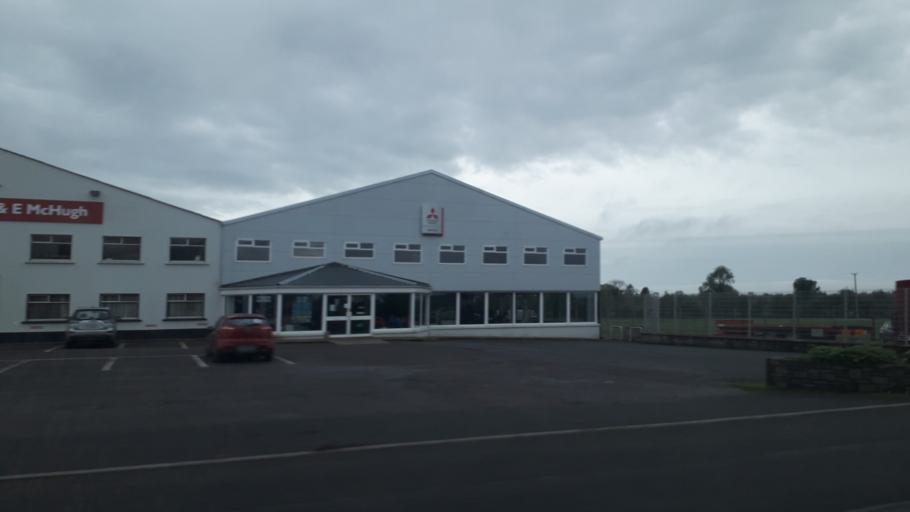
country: IE
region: Leinster
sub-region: An Longfort
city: Longford
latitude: 53.7258
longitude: -7.8738
